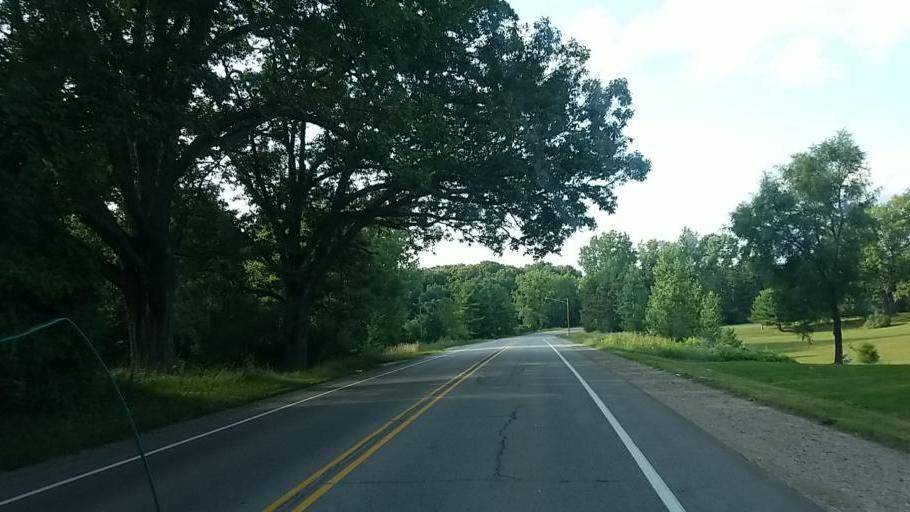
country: US
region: Michigan
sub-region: Kent County
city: Lowell
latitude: 42.8986
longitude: -85.3711
